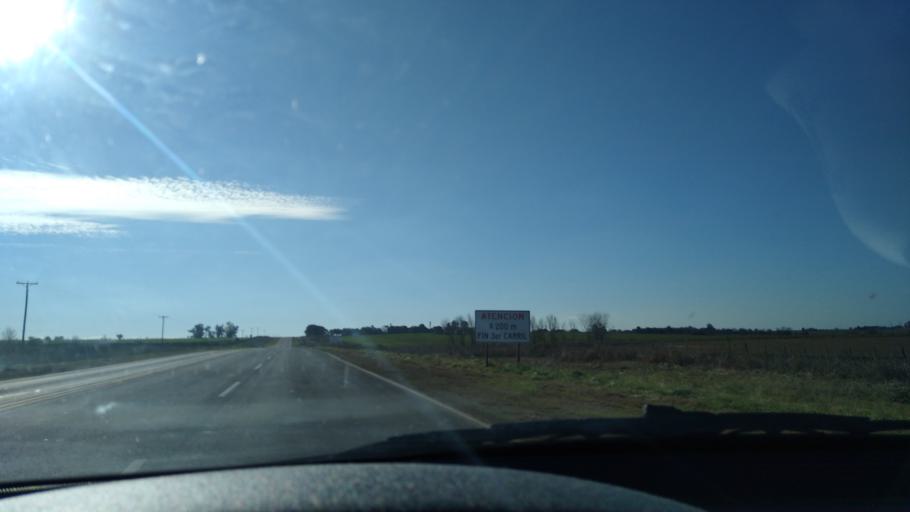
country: AR
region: Entre Rios
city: Aranguren
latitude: -32.3984
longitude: -60.3274
